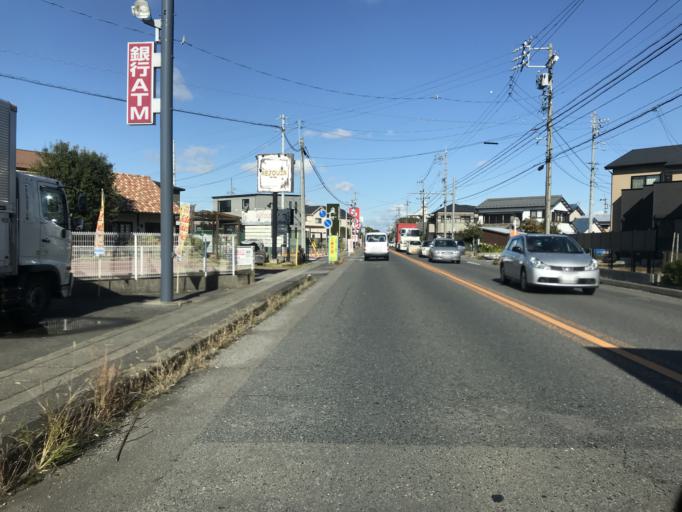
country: JP
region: Aichi
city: Inazawa
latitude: 35.2223
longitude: 136.8416
